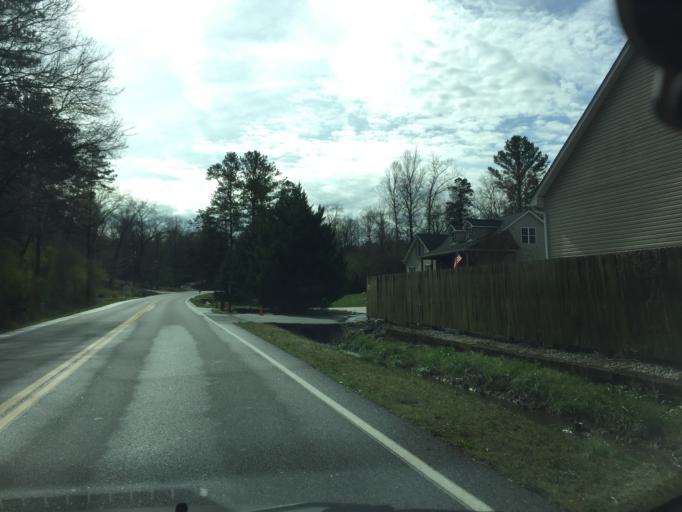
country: US
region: Tennessee
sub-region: Hamilton County
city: East Brainerd
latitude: 35.0384
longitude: -85.1103
